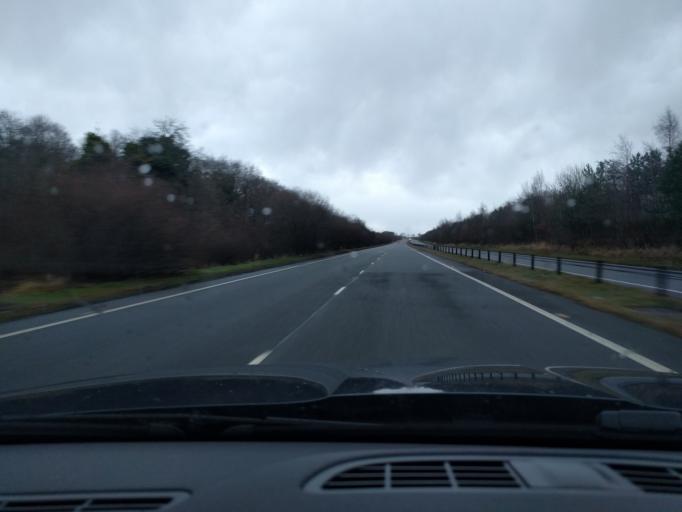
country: GB
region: Scotland
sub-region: East Lothian
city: Haddington
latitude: 55.9719
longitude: -2.7242
